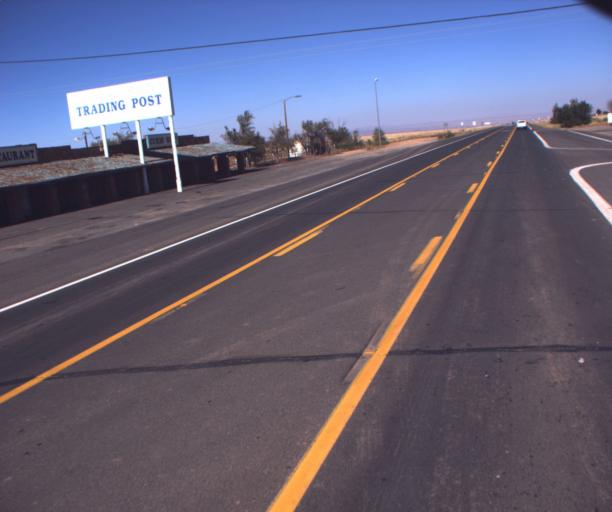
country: US
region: Arizona
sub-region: Coconino County
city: Tuba City
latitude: 35.7453
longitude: -111.4737
